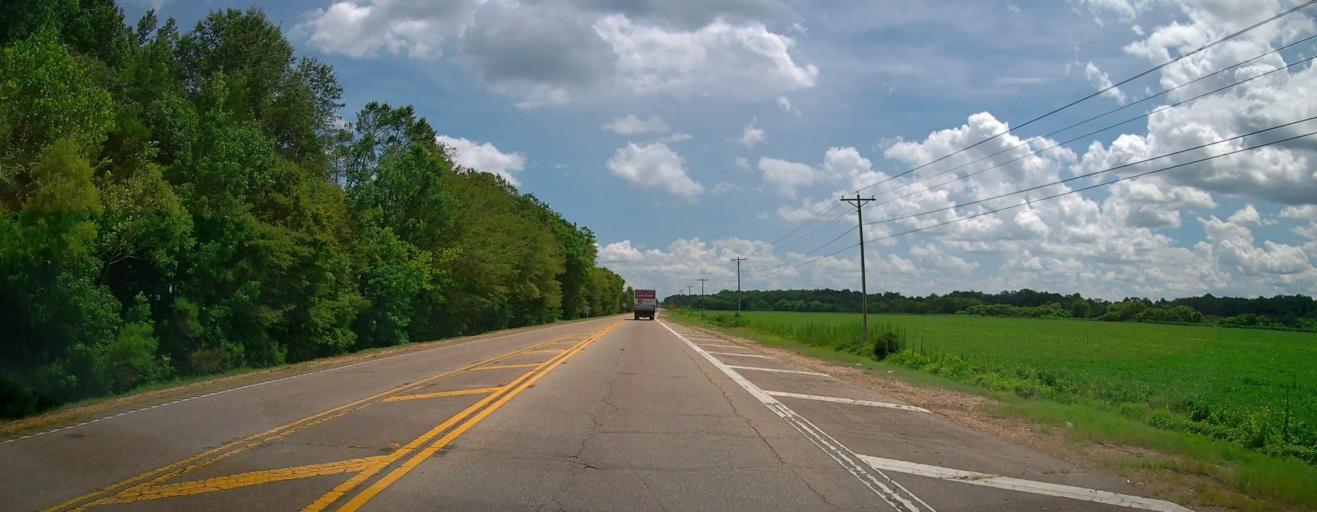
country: US
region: Mississippi
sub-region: Lee County
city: Shannon
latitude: 34.1488
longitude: -88.7194
